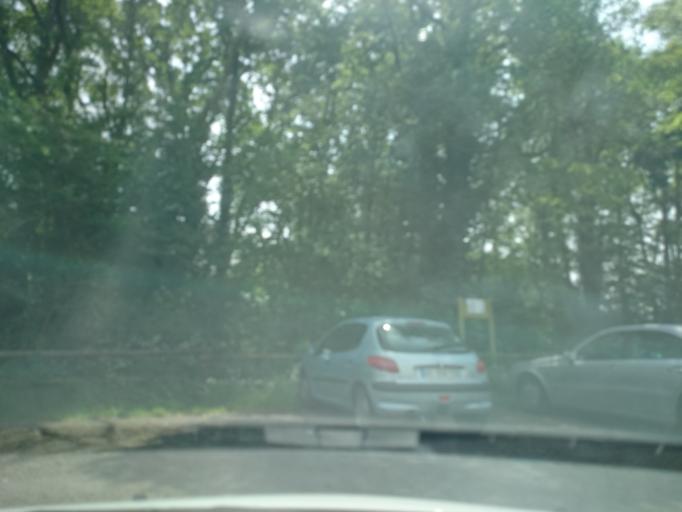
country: FR
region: Pays de la Loire
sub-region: Departement de la Loire-Atlantique
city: Bouaye
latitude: 47.1223
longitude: -1.6521
